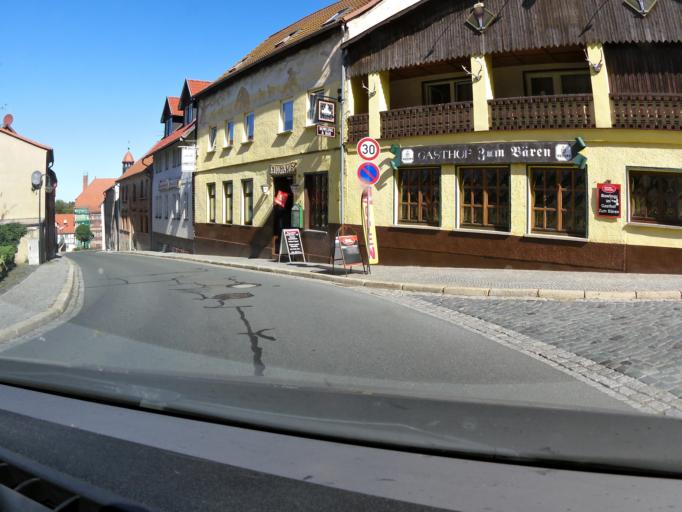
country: DE
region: Saxony-Anhalt
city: Gernrode
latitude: 51.7233
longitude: 11.1410
